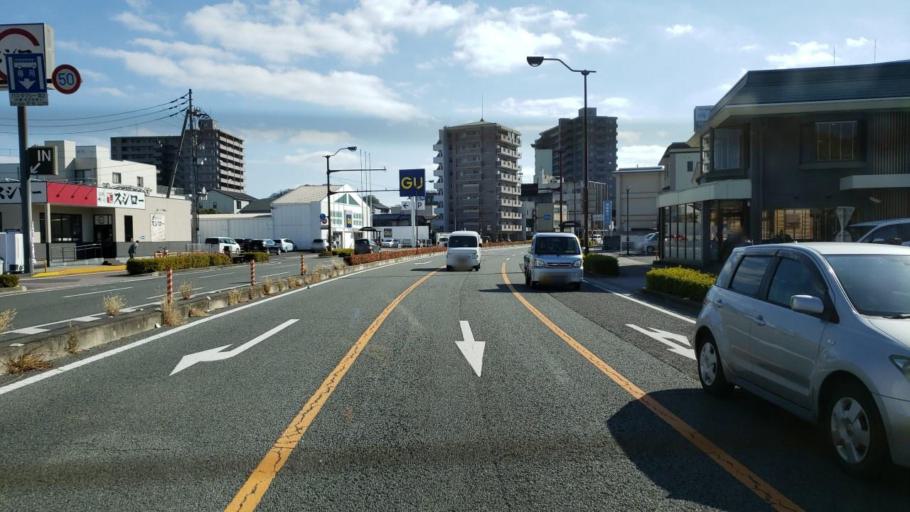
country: JP
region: Tokushima
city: Tokushima-shi
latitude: 34.0769
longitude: 134.5444
